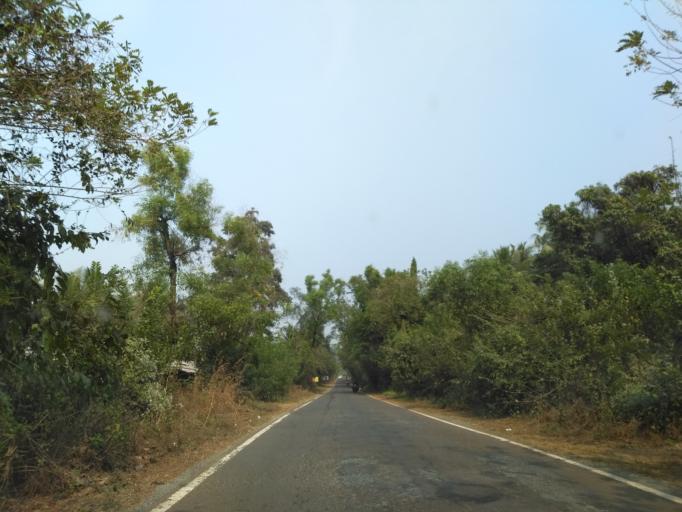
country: IN
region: Goa
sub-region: North Goa
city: Dicholi
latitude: 15.7253
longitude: 73.9526
